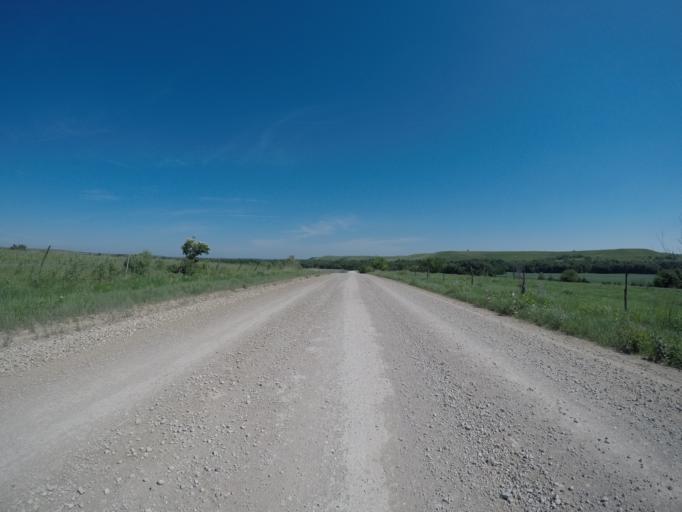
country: US
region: Kansas
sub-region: Wabaunsee County
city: Alma
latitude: 39.0177
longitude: -96.1413
